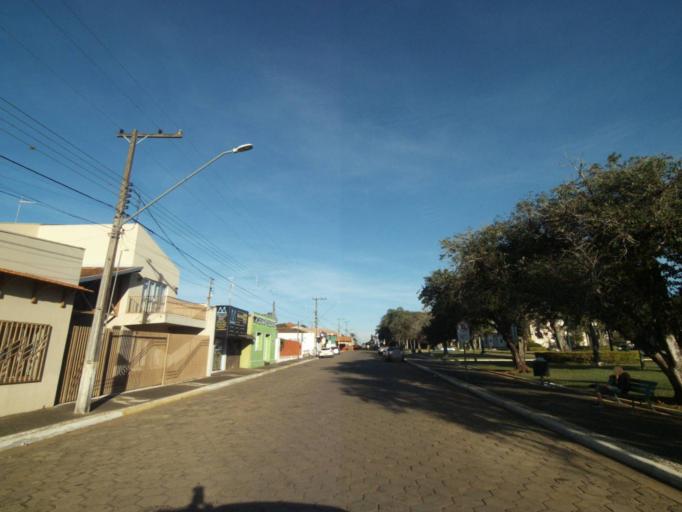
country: BR
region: Parana
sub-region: Tibagi
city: Tibagi
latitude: -24.5143
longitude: -50.4103
